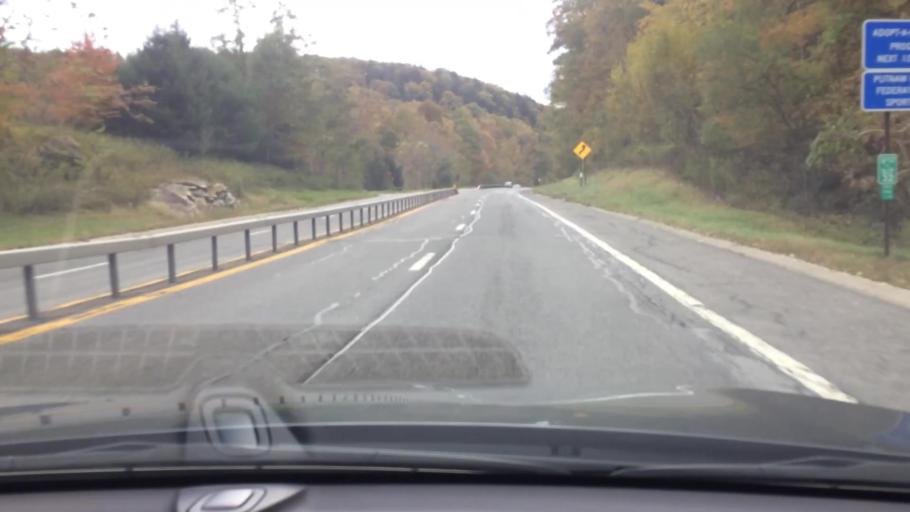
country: US
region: New York
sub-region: Dutchess County
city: Brinckerhoff
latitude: 41.4769
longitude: -73.8194
